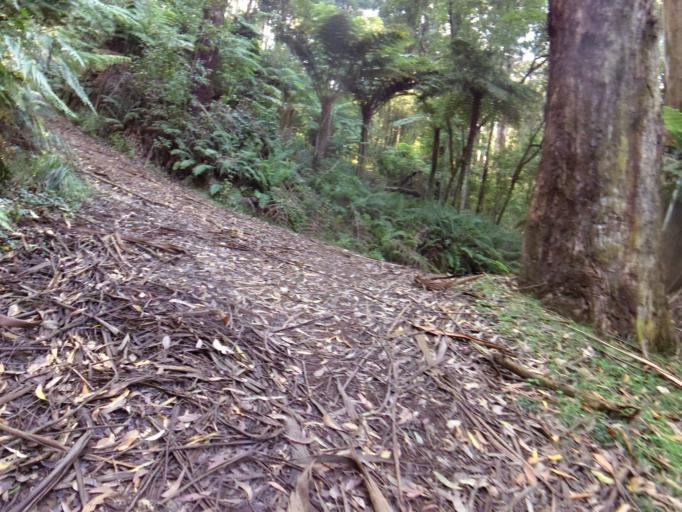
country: AU
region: Victoria
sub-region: Yarra Ranges
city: Olinda
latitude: -37.8417
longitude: 145.3493
